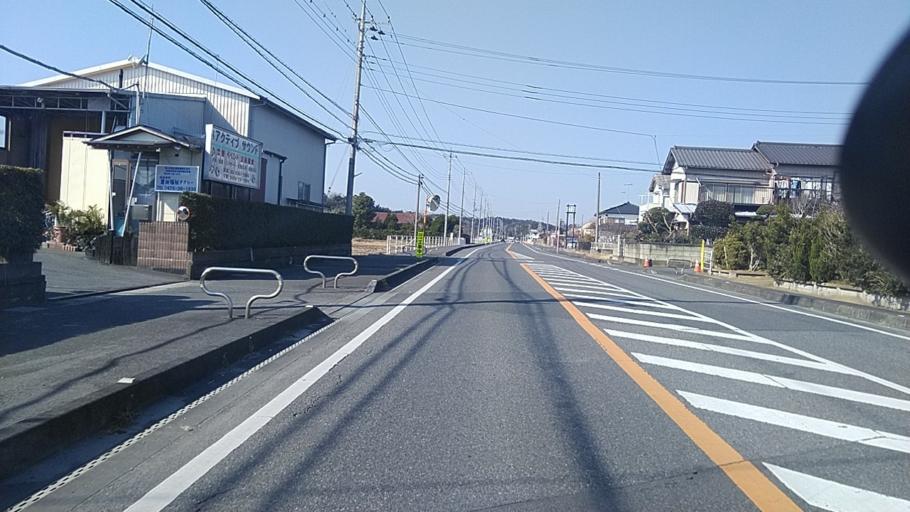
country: JP
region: Chiba
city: Mobara
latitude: 35.4546
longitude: 140.2896
